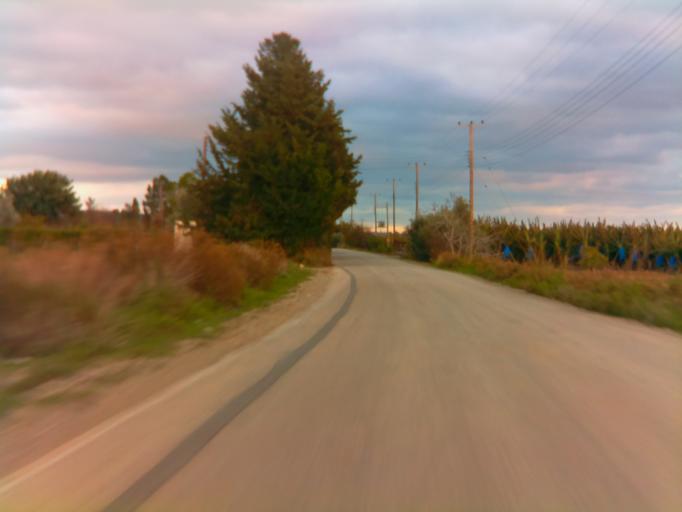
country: CY
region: Pafos
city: Pegeia
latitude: 34.8659
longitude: 32.3516
